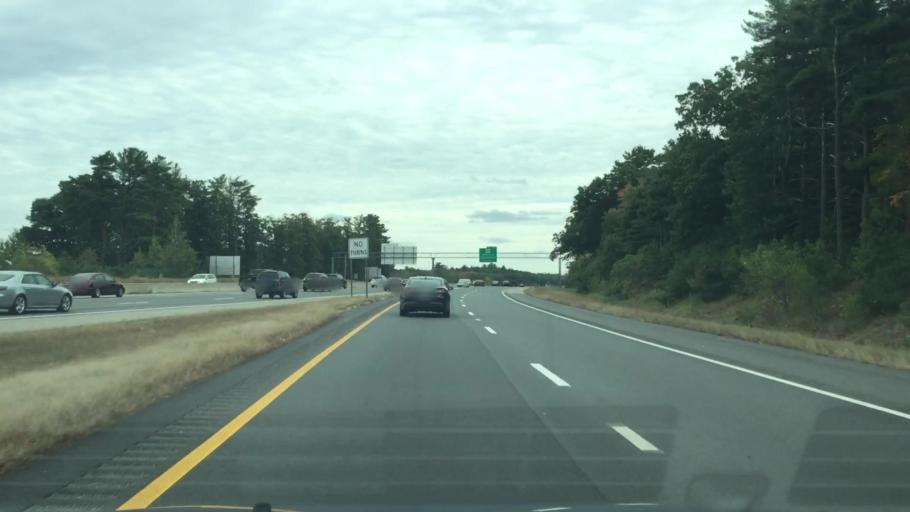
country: US
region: Massachusetts
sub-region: Middlesex County
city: Lowell
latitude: 42.5952
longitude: -71.3183
